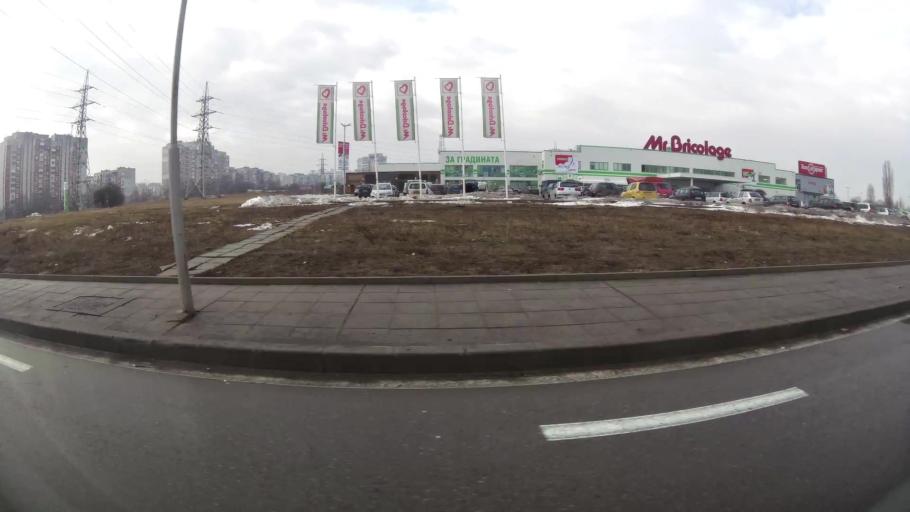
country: BG
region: Sofiya
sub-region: Obshtina Bozhurishte
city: Bozhurishte
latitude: 42.7339
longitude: 23.2494
